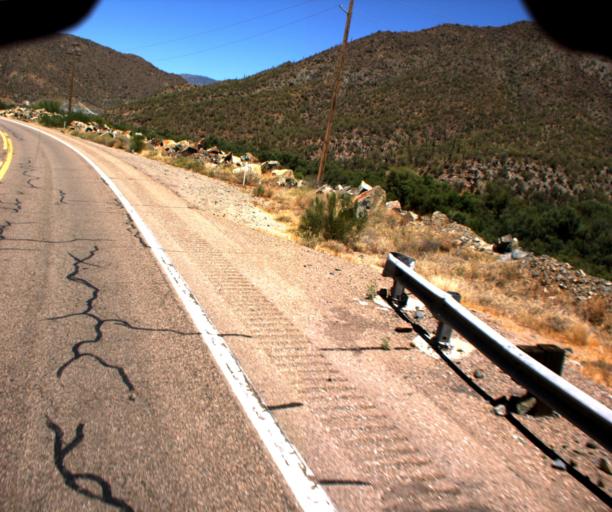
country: US
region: Arizona
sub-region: Pinal County
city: Kearny
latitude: 33.0569
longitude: -110.7195
